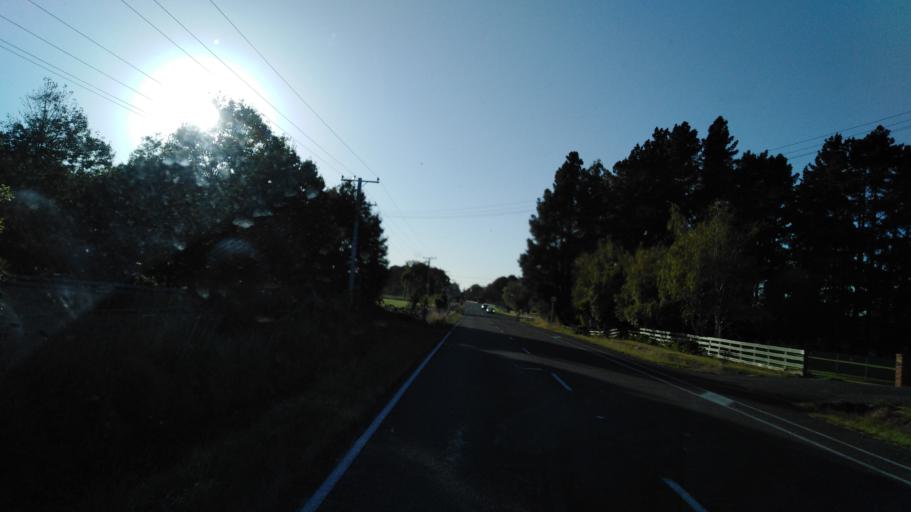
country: NZ
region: Manawatu-Wanganui
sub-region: Rangitikei District
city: Bulls
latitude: -40.0656
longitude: 175.3931
